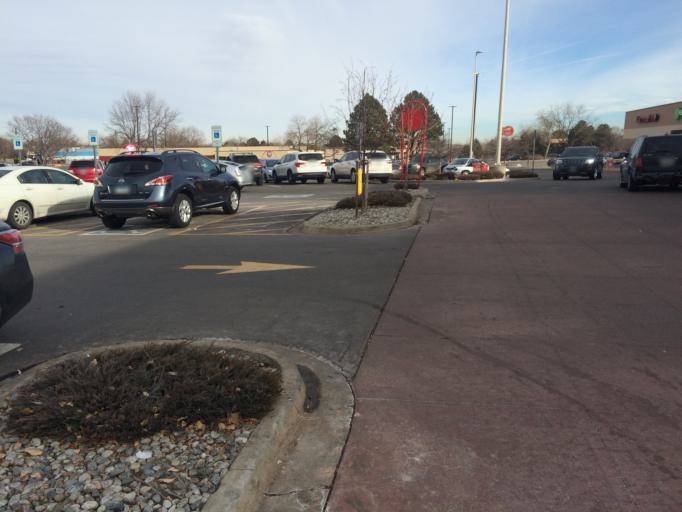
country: US
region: Colorado
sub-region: Jefferson County
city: Arvada
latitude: 39.8402
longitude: -105.0851
